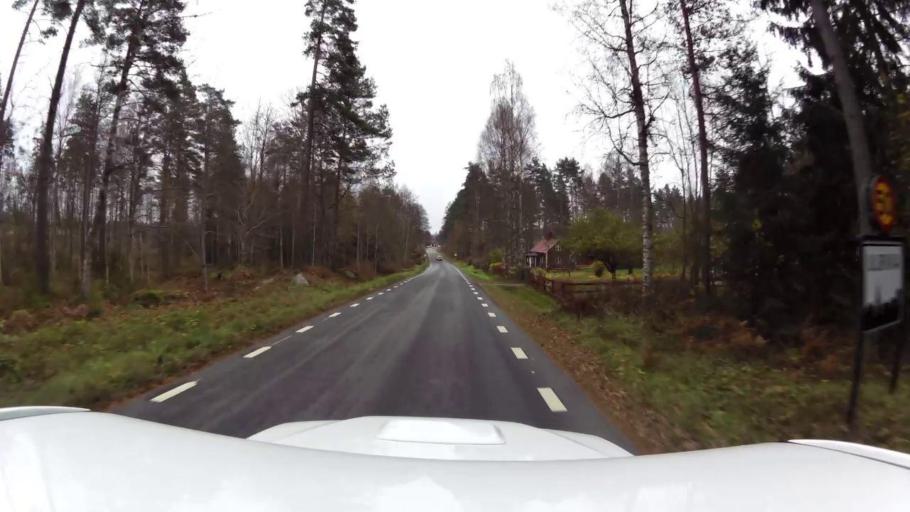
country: SE
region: OEstergoetland
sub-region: Kinda Kommun
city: Kisa
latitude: 58.1301
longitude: 15.4271
